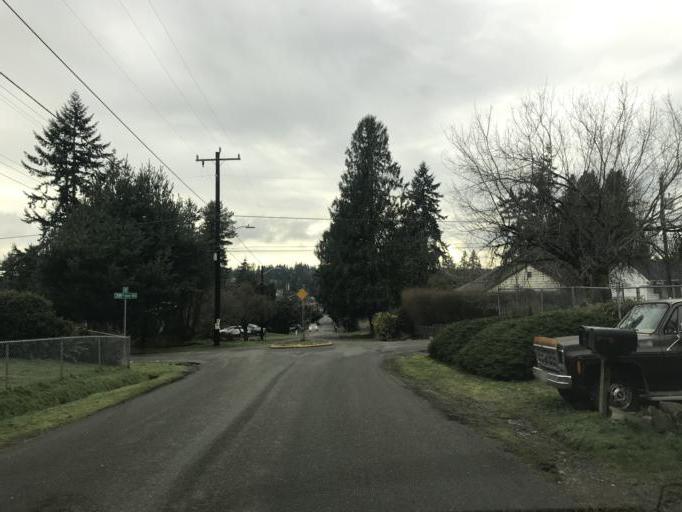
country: US
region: Washington
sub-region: King County
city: Lake Forest Park
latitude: 47.7173
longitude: -122.2868
